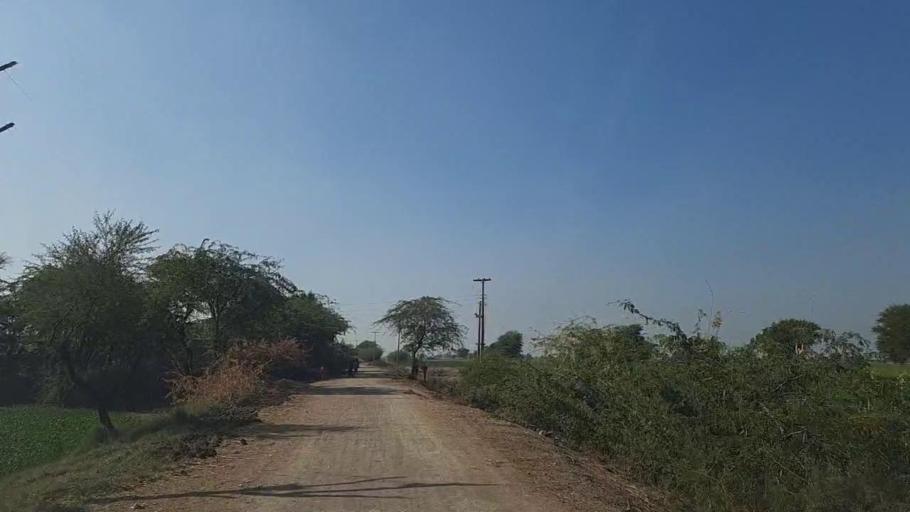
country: PK
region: Sindh
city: Shahpur Chakar
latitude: 26.1953
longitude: 68.6109
